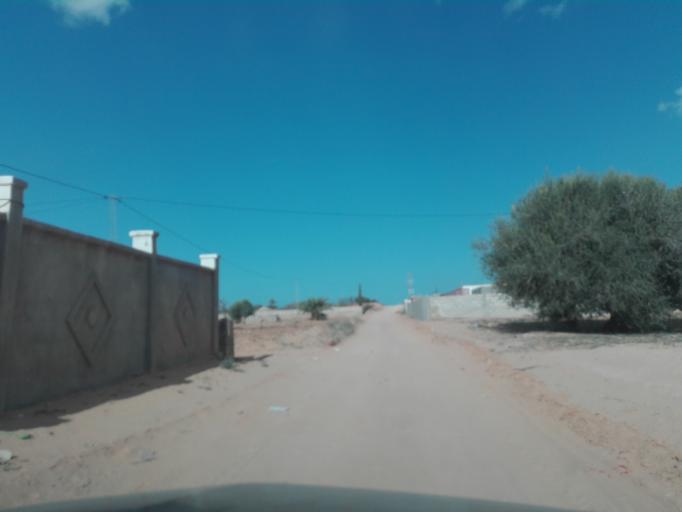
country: TN
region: Madanin
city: Bin Qirdan
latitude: 33.1629
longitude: 11.1956
